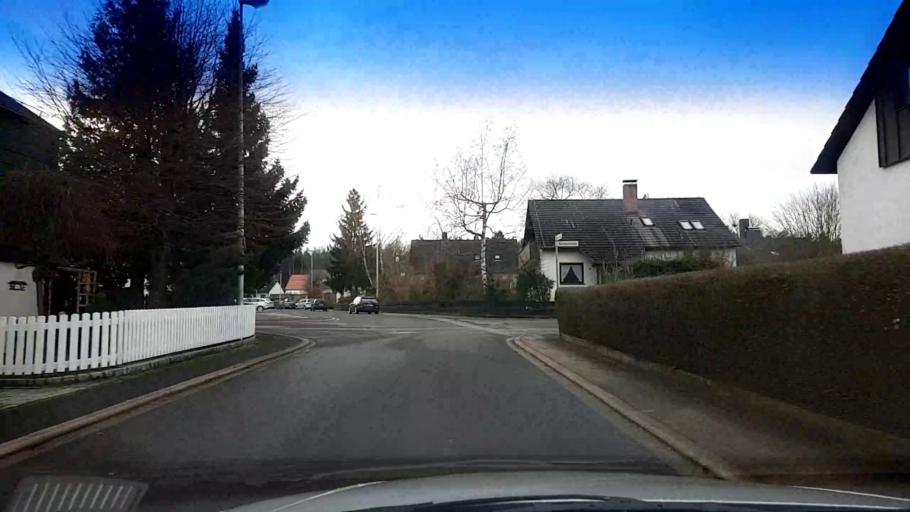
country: DE
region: Bavaria
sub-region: Upper Franconia
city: Litzendorf
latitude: 49.9099
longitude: 10.9850
